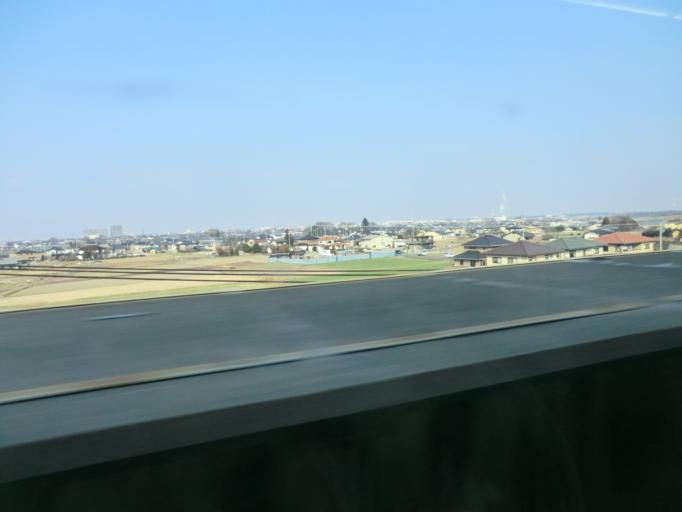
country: JP
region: Gunma
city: Fujioka
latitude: 36.2856
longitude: 139.0464
